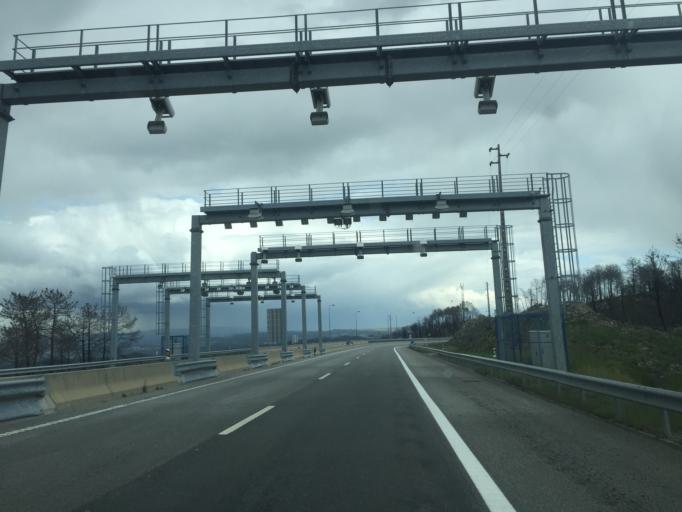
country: PT
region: Viseu
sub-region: Vouzela
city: Vouzela
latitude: 40.6950
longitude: -8.0868
